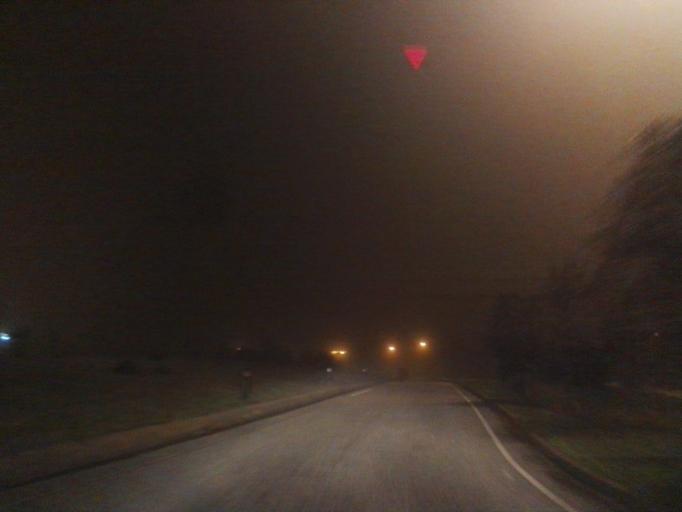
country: PT
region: Evora
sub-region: Montemor-O-Novo
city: Montemor-o-Novo
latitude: 38.6172
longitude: -8.0801
